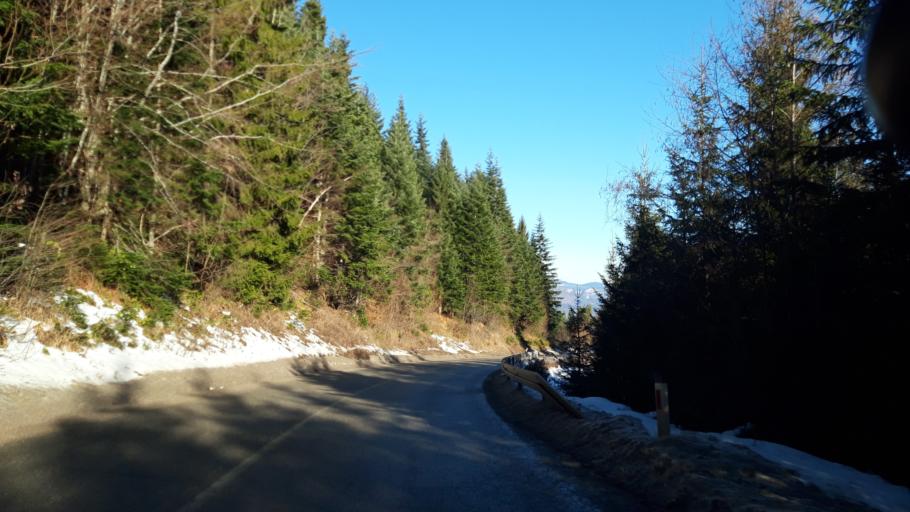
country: BA
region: Republika Srpska
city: Koran
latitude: 43.7954
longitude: 18.5553
